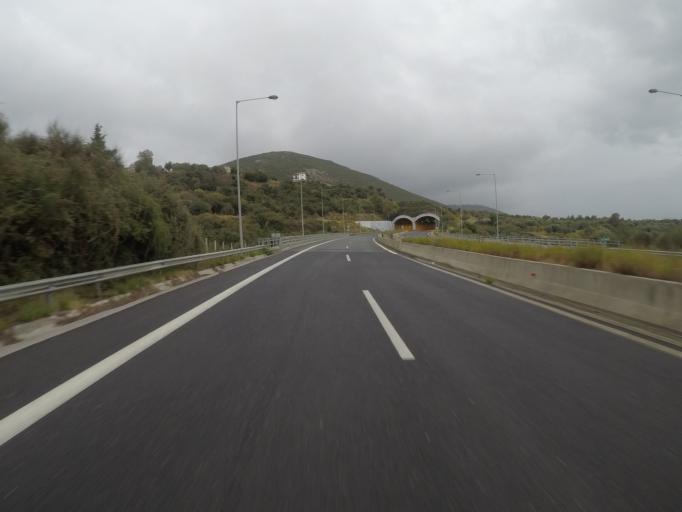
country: GR
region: Peloponnese
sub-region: Nomos Arkadias
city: Megalopoli
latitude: 37.3942
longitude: 22.1817
